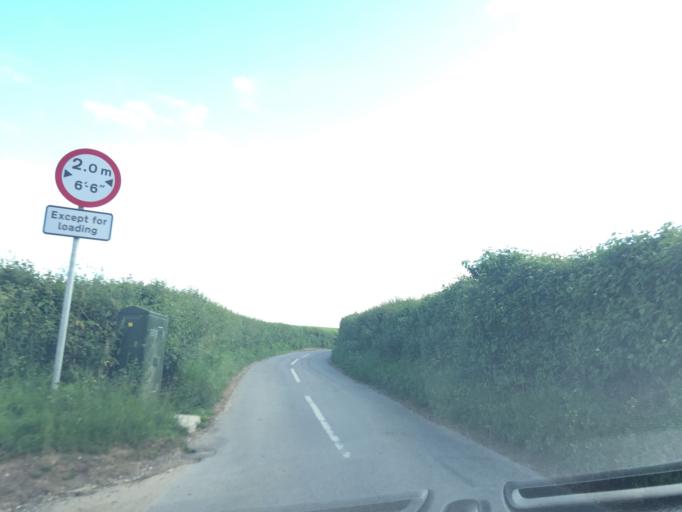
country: GB
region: England
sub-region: Dorset
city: Bovington Camp
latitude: 50.7335
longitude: -2.3285
